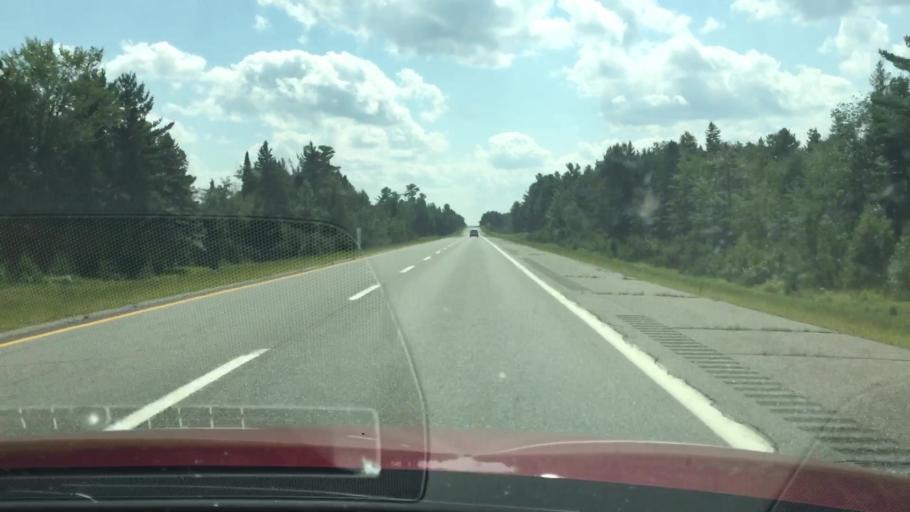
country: US
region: Maine
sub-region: Penobscot County
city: Lincoln
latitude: 45.4028
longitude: -68.5985
